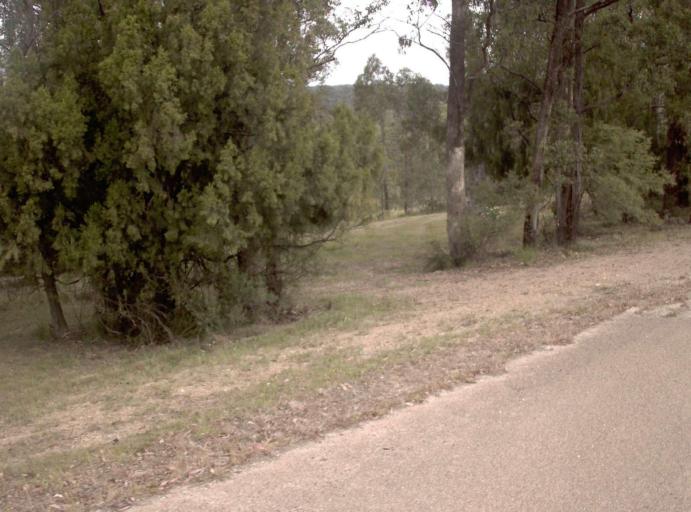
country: AU
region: Victoria
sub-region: East Gippsland
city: Lakes Entrance
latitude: -37.7271
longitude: 148.0884
